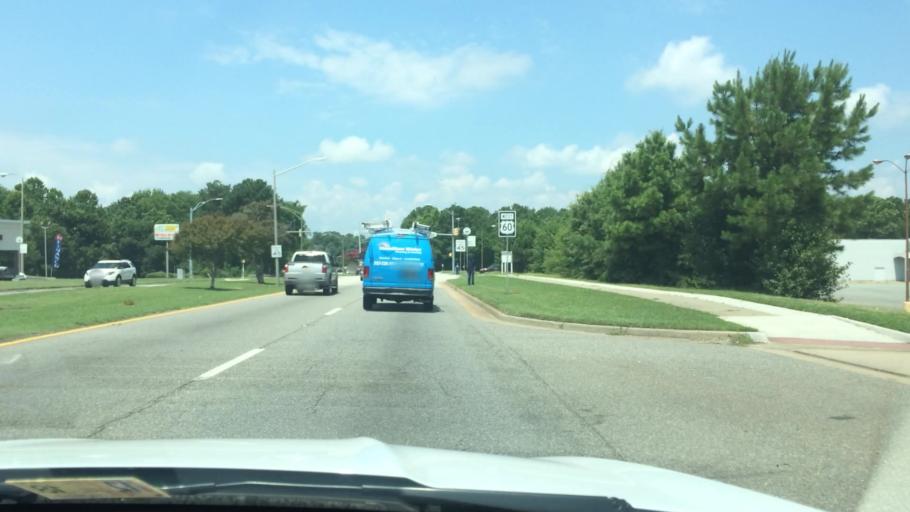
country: US
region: Virginia
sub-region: York County
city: Yorktown
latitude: 37.1303
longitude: -76.5386
